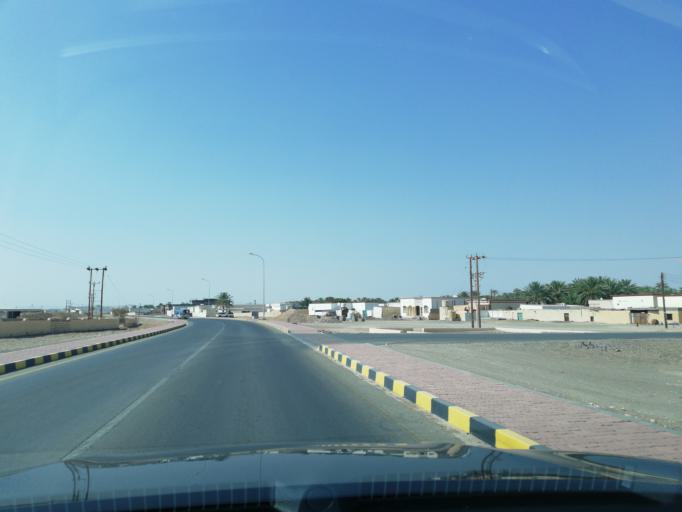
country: OM
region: Muhafazat ad Dakhiliyah
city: Adam
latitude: 22.3036
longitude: 58.0721
